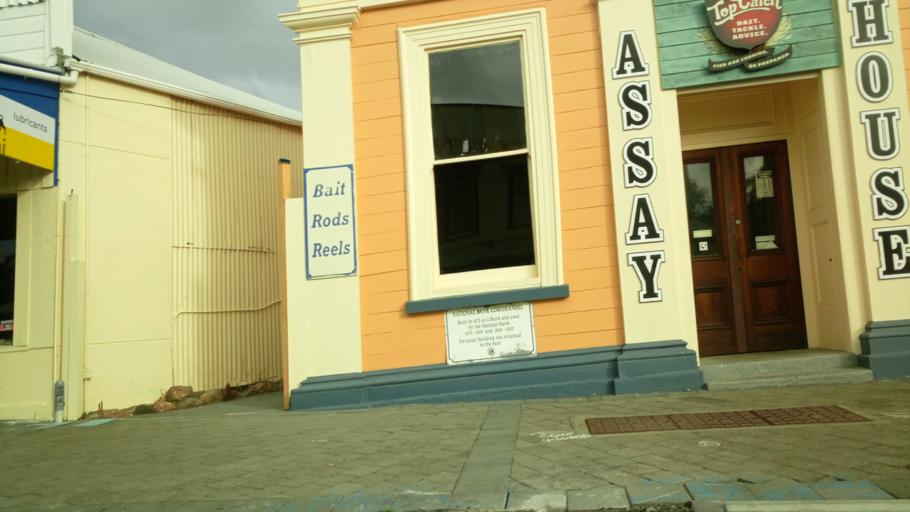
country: NZ
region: Waikato
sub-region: Thames-Coromandel District
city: Coromandel
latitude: -36.7601
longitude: 175.4974
